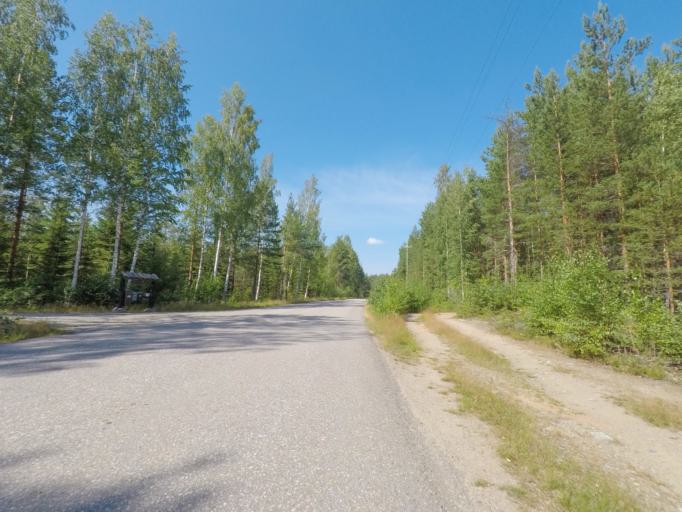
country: FI
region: Southern Savonia
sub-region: Mikkeli
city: Puumala
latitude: 61.4389
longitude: 28.1663
